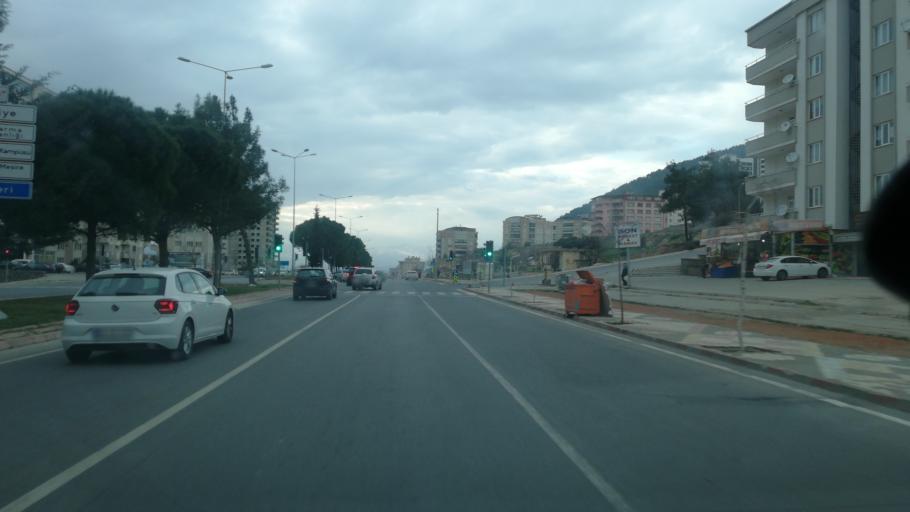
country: TR
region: Kahramanmaras
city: Kahramanmaras
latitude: 37.5955
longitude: 36.8522
